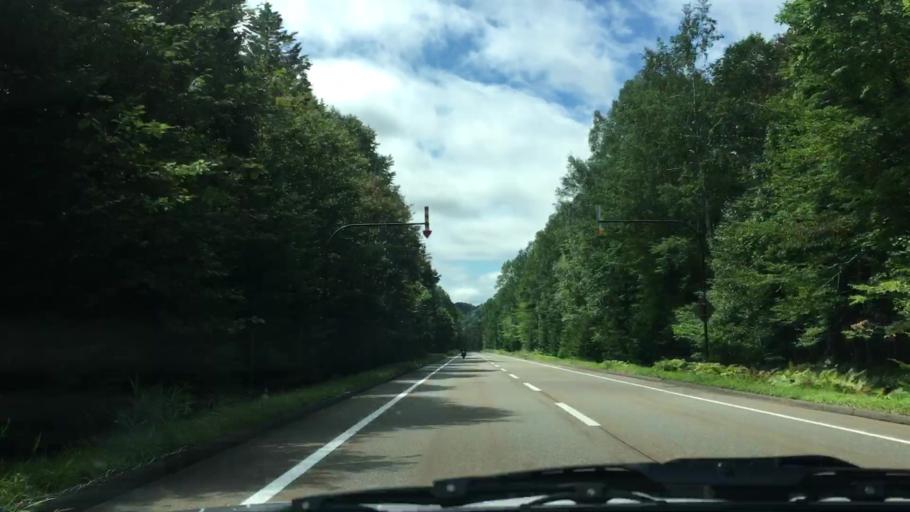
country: JP
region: Hokkaido
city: Kitami
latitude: 43.4034
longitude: 143.9327
